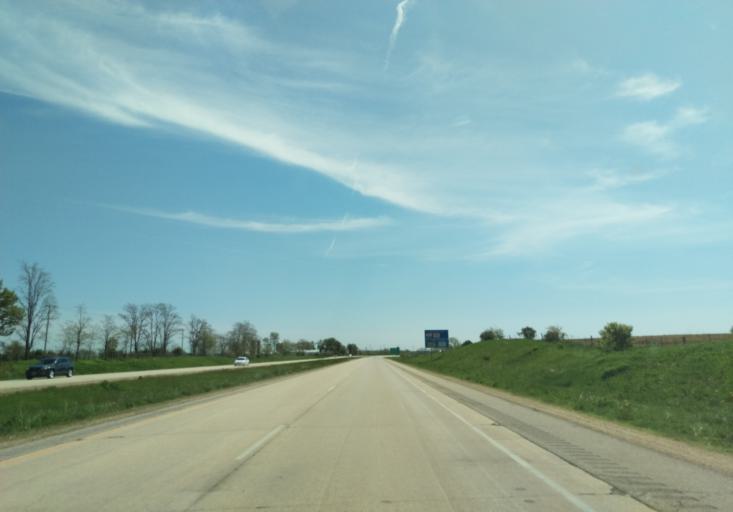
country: US
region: Wisconsin
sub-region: Dane County
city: Mount Horeb
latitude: 43.0066
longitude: -89.7798
